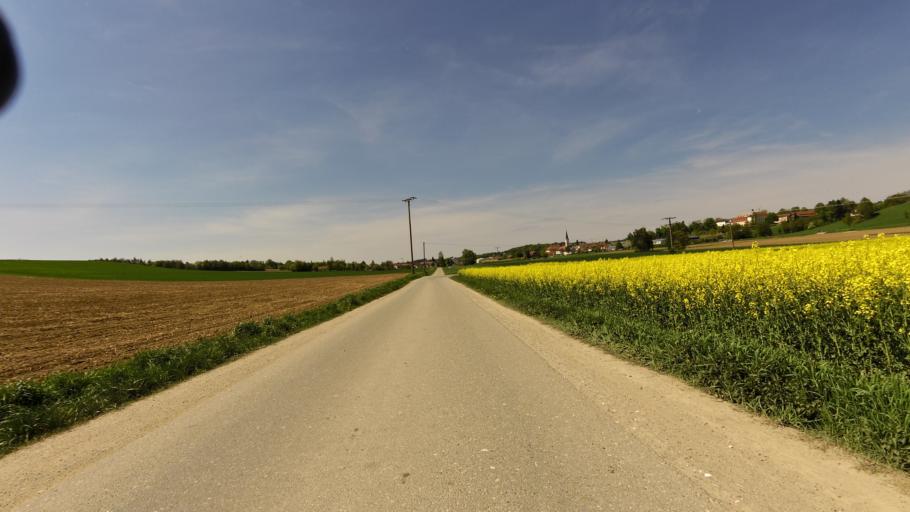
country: DE
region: Bavaria
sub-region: Lower Bavaria
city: Furth
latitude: 48.5871
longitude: 12.0354
